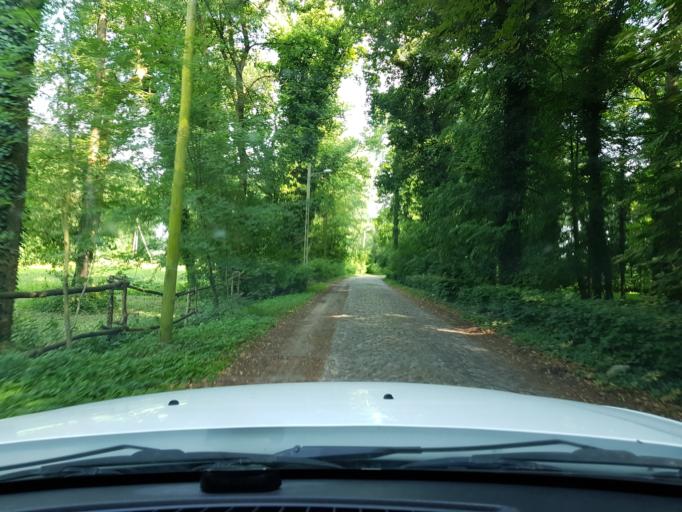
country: PL
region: West Pomeranian Voivodeship
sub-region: Powiat gryfinski
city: Chojna
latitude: 52.9974
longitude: 14.4845
